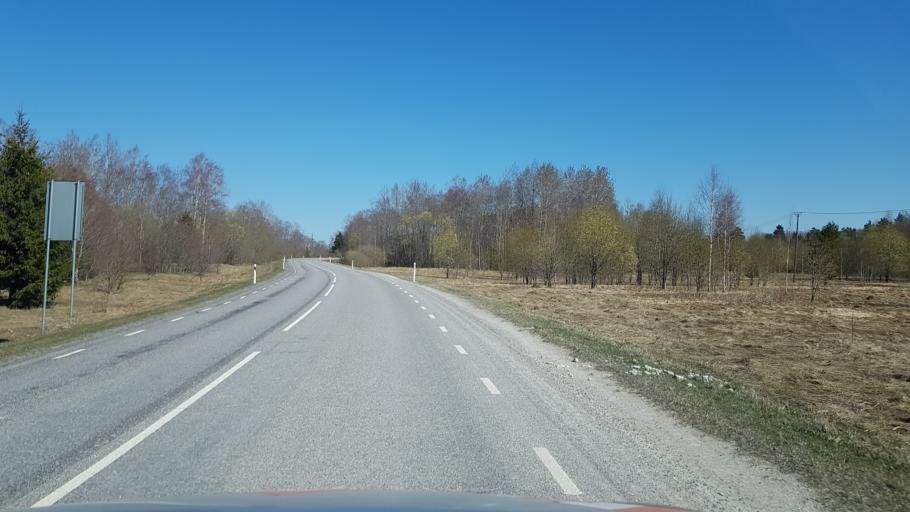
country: EE
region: Ida-Virumaa
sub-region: Kohtla-Jaerve linn
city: Kohtla-Jarve
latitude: 59.3308
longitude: 27.2752
